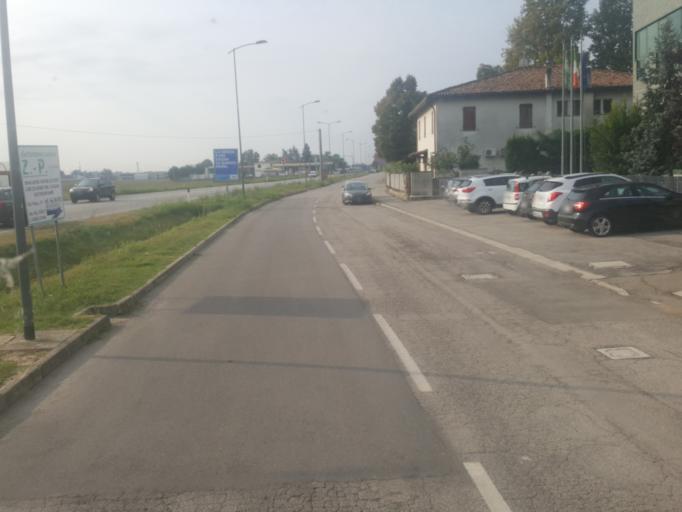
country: IT
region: Emilia-Romagna
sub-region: Provincia di Bologna
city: San Giorgio di Piano
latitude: 44.6178
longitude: 11.3705
